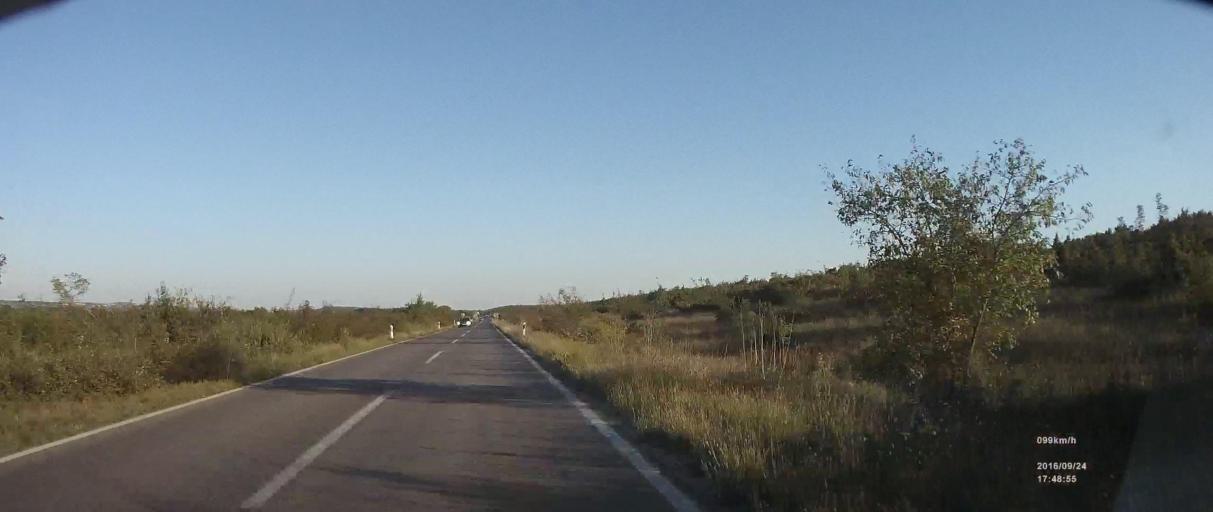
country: HR
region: Zadarska
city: Polaca
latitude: 44.0595
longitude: 15.5429
